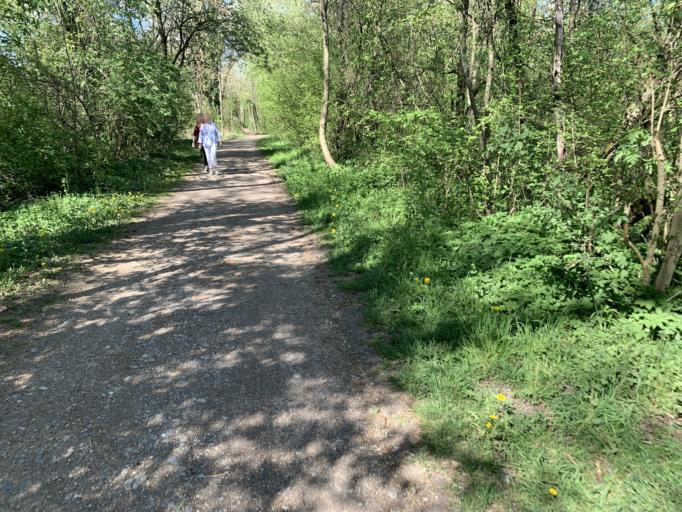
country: DE
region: Bavaria
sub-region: Swabia
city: Gersthofen
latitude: 48.4320
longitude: 10.8919
